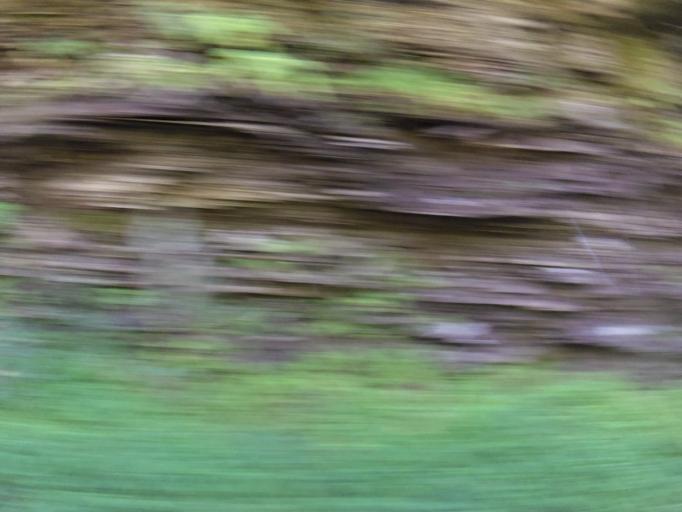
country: US
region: Kentucky
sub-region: Leslie County
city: Hyden
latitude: 37.1628
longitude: -83.5563
